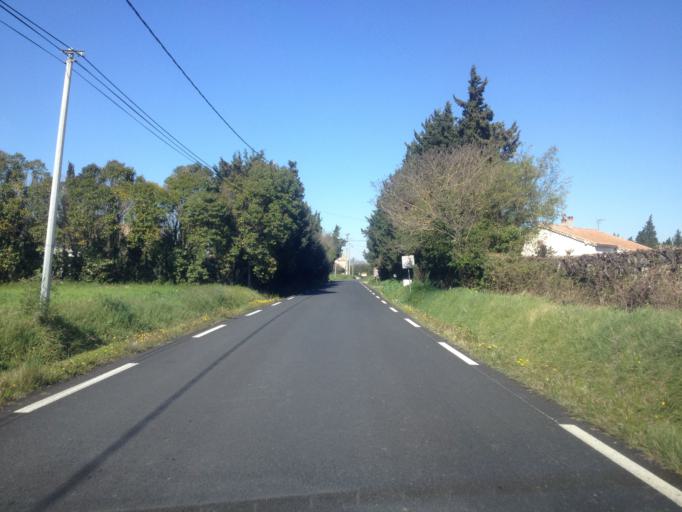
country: FR
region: Provence-Alpes-Cote d'Azur
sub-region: Departement du Vaucluse
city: Orange
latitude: 44.1503
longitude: 4.8125
